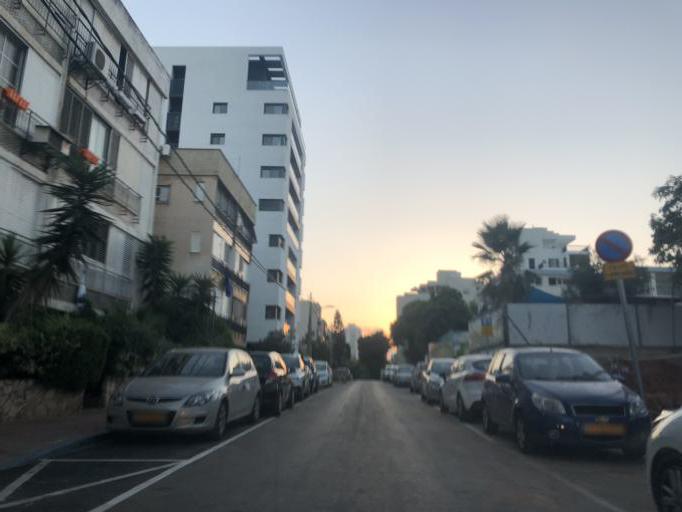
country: IL
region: Tel Aviv
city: Giv`atayim
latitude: 32.0643
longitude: 34.8259
